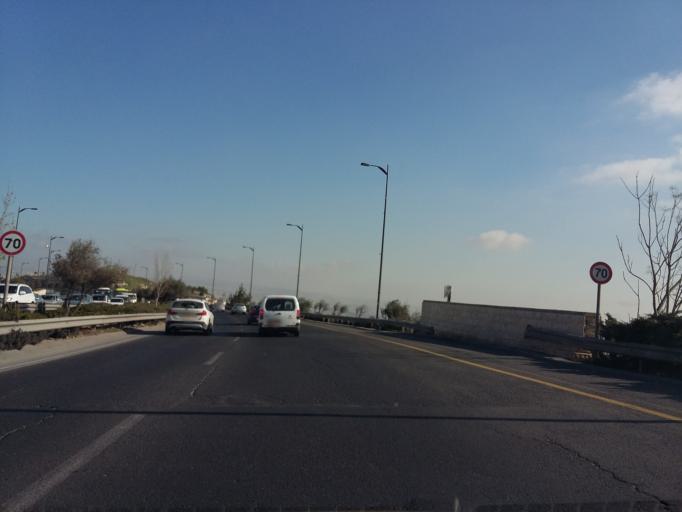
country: PS
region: West Bank
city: `Anata
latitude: 31.8115
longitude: 35.2385
